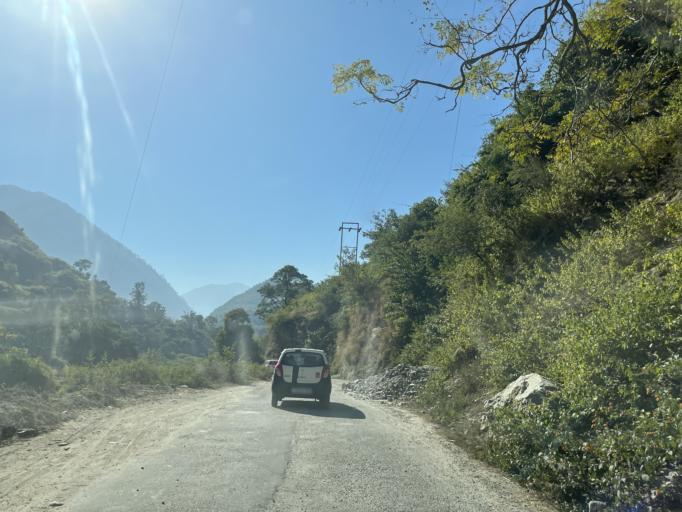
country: IN
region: Uttarakhand
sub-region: Naini Tal
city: Naini Tal
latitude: 29.5152
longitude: 79.4773
